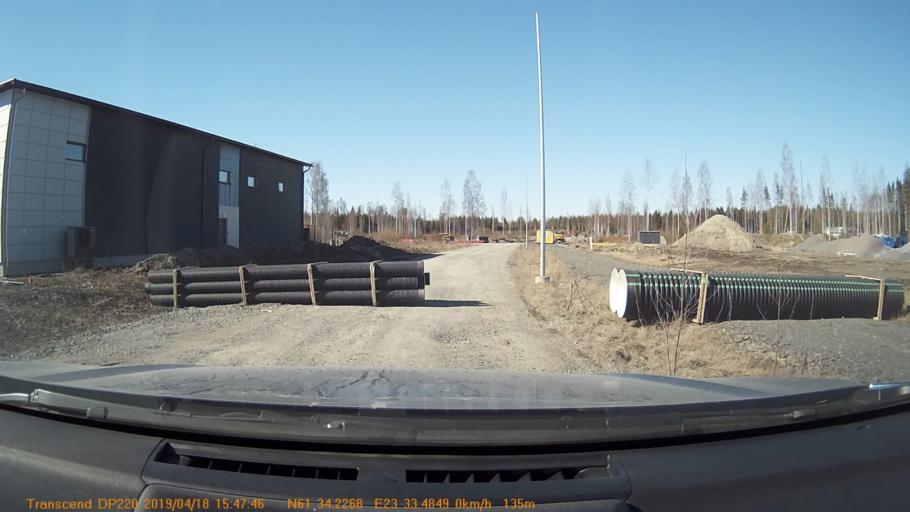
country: FI
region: Pirkanmaa
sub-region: Tampere
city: Yloejaervi
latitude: 61.5704
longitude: 23.5582
